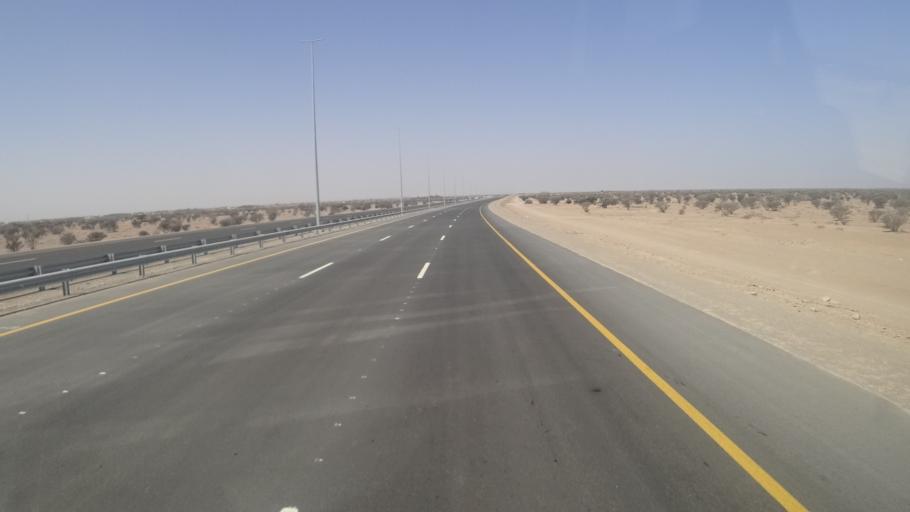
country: OM
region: Ash Sharqiyah
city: Sur
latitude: 22.2719
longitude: 59.2442
